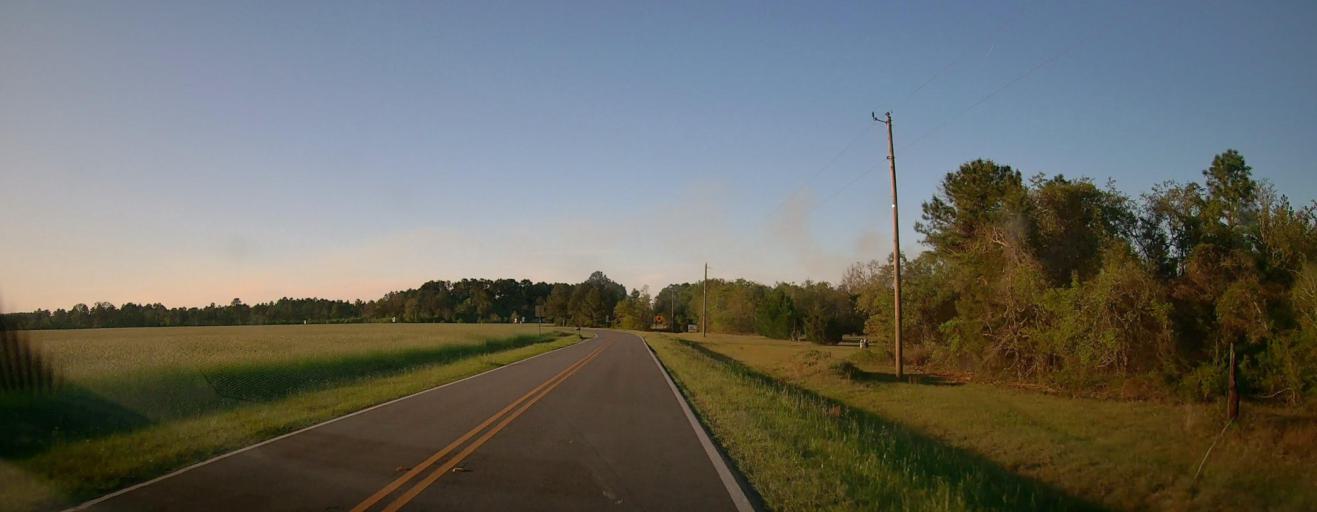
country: US
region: Georgia
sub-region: Marion County
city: Buena Vista
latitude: 32.4572
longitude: -84.4252
